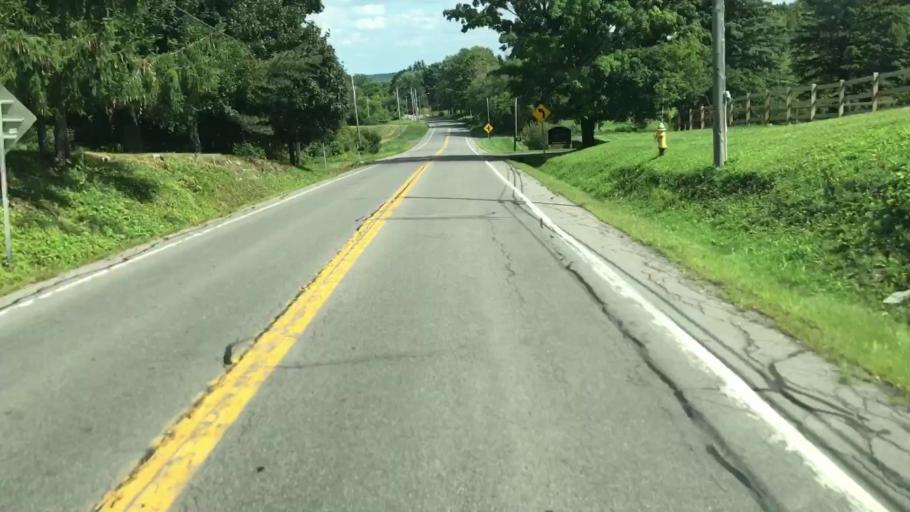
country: US
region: New York
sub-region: Onondaga County
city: Camillus
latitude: 42.9832
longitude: -76.2780
